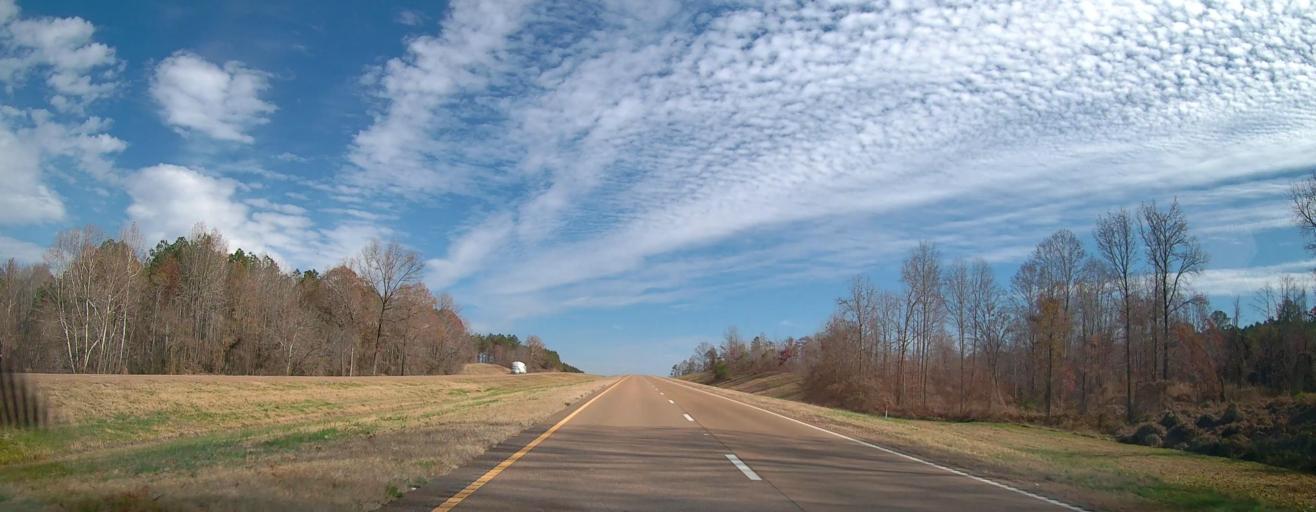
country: US
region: Mississippi
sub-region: Benton County
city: Ashland
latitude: 34.9486
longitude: -89.1039
